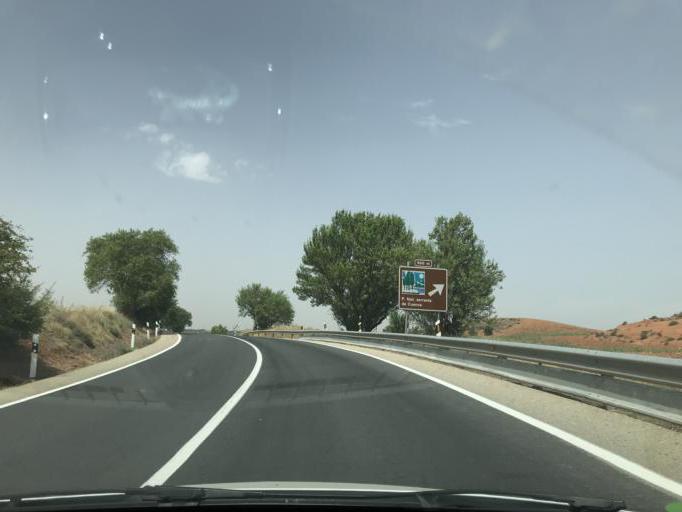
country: ES
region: Castille-La Mancha
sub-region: Provincia de Cuenca
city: Villar de Domingo Garcia
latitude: 40.2433
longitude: -2.2962
